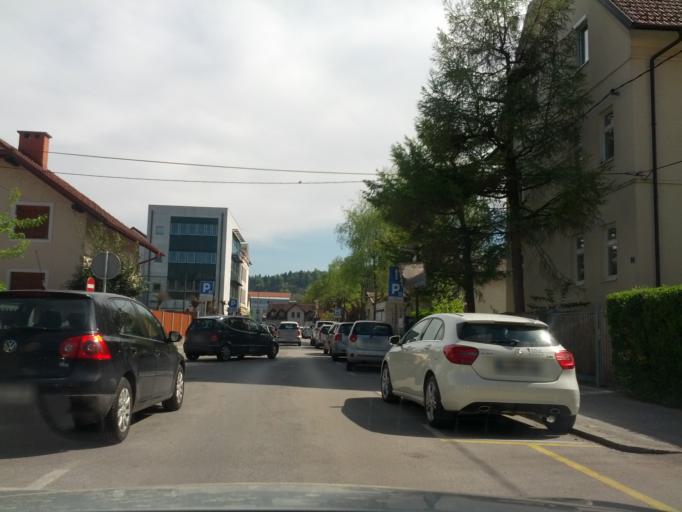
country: SI
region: Ljubljana
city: Ljubljana
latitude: 46.0565
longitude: 14.5309
